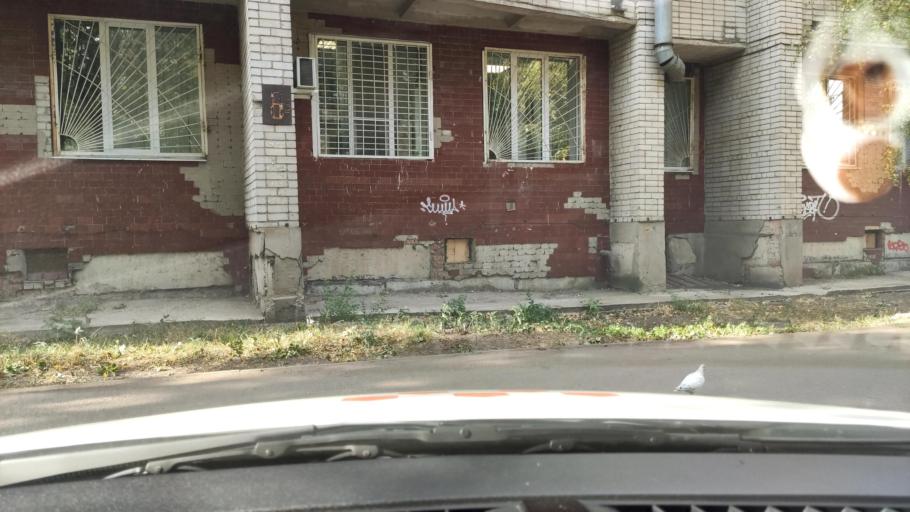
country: RU
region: Voronezj
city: Voronezh
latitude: 51.6848
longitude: 39.1980
